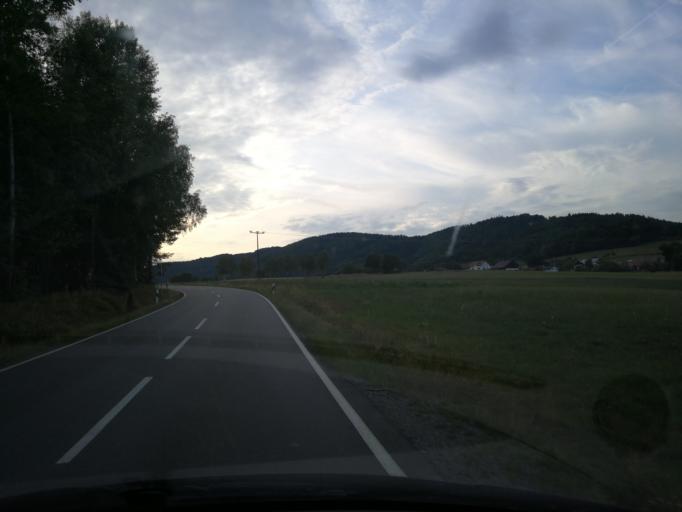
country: DE
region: Bavaria
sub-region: Lower Bavaria
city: Haibach
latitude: 49.0320
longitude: 12.7046
